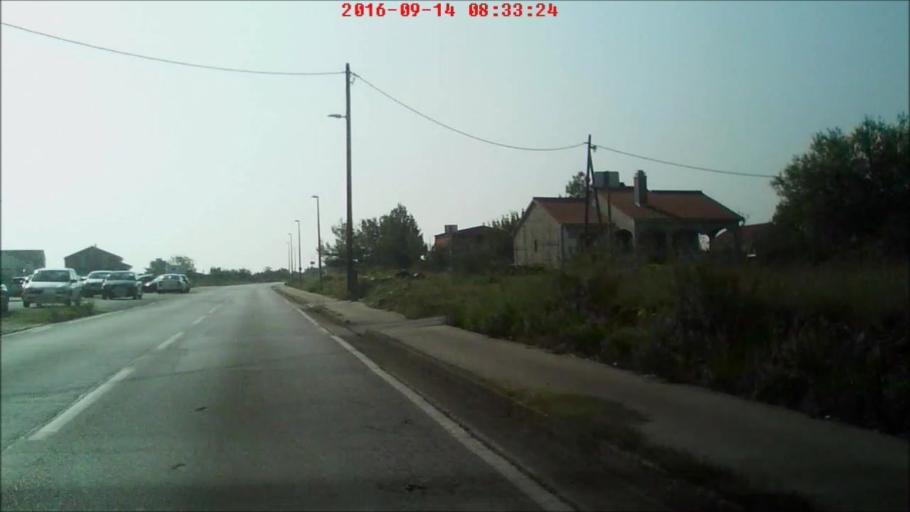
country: HR
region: Zadarska
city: Policnik
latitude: 44.1566
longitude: 15.3120
